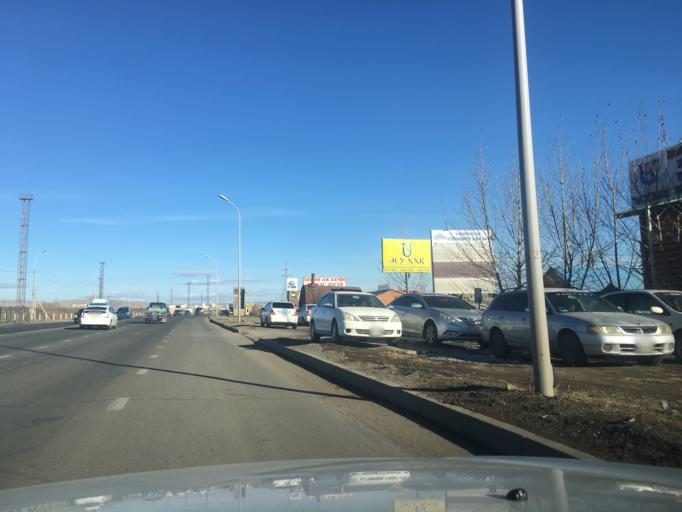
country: MN
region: Ulaanbaatar
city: Ulaanbaatar
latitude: 47.9032
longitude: 106.7452
